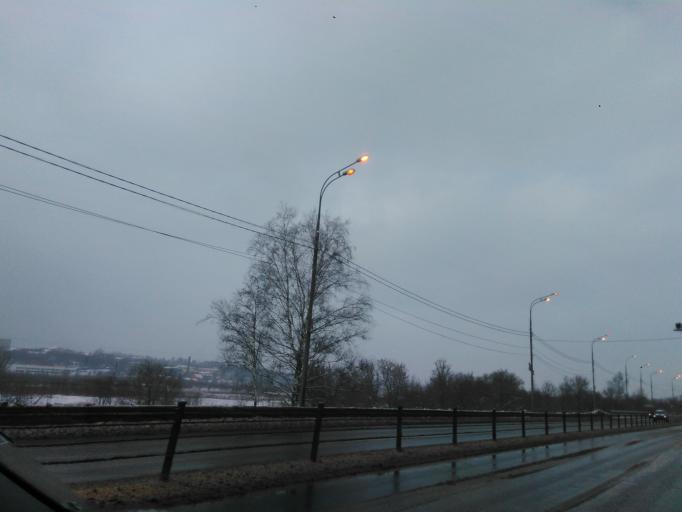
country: RU
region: Moskovskaya
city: Dedenevo
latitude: 56.2720
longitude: 37.5028
